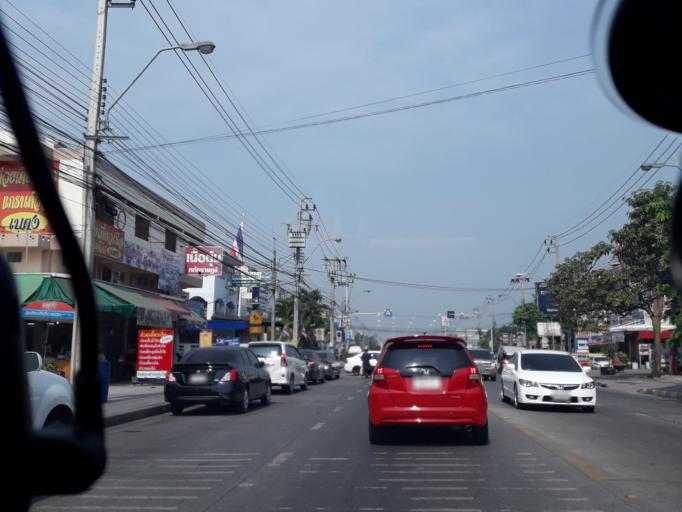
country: TH
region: Bangkok
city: Khlong Sam Wa
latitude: 13.8284
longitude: 100.7202
